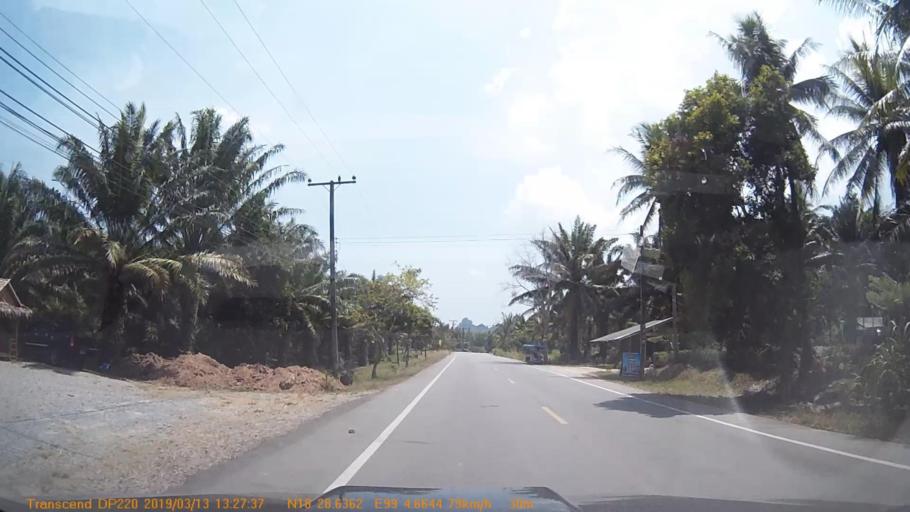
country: TH
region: Chumphon
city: Chumphon
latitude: 10.4827
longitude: 99.0770
